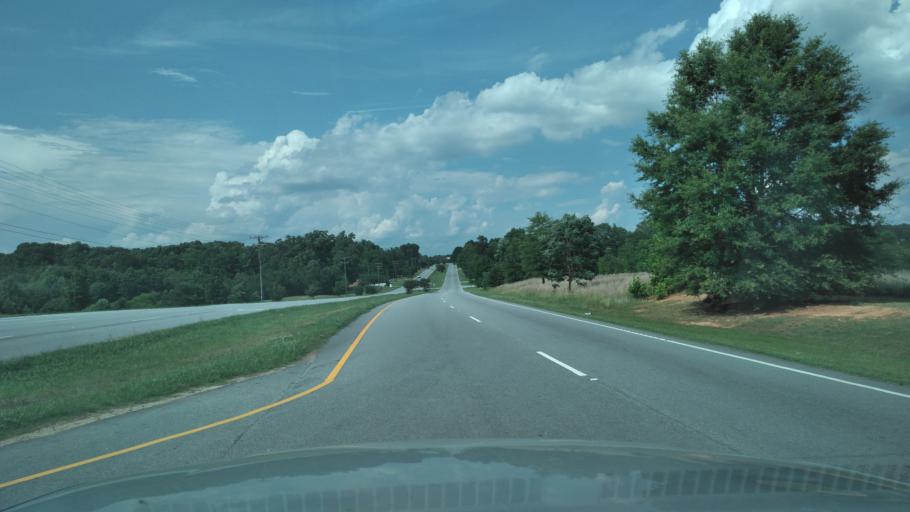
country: US
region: South Carolina
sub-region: Spartanburg County
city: Roebuck
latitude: 34.8543
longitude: -81.9660
